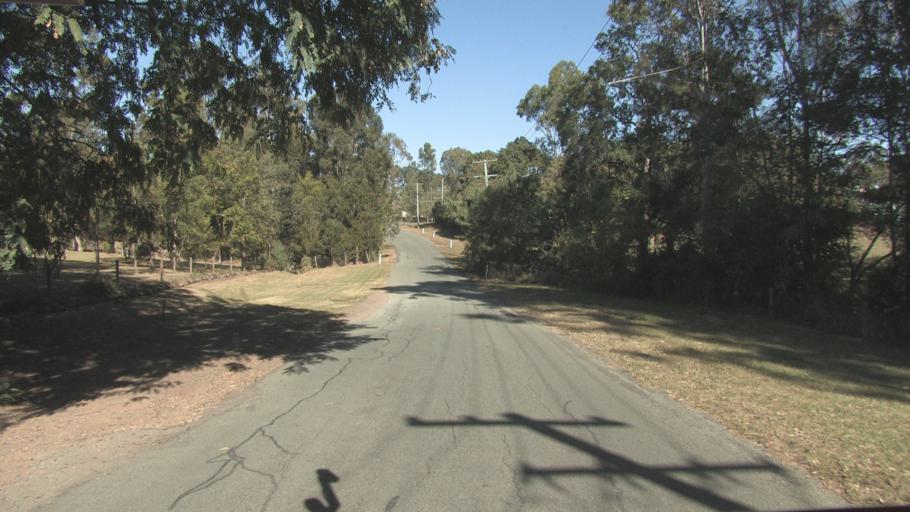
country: AU
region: Queensland
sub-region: Logan
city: Cedar Vale
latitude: -27.8519
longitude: 152.9869
